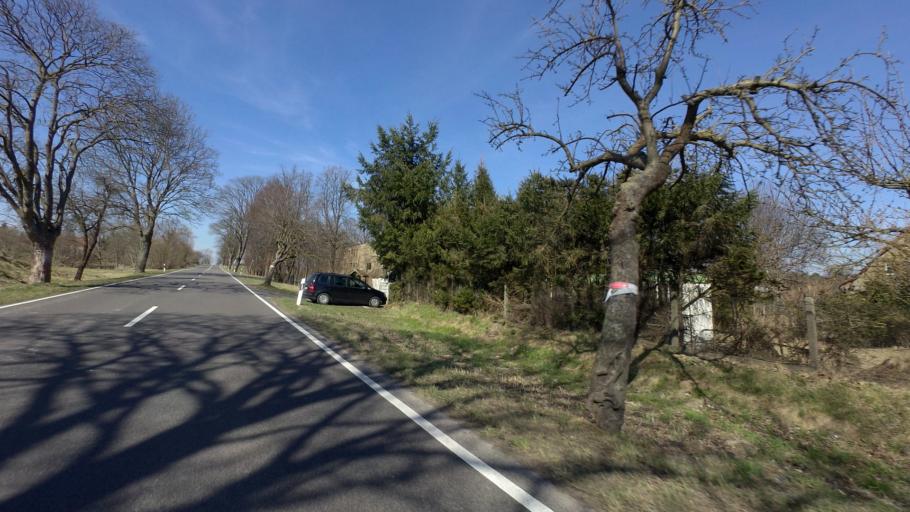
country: DE
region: Brandenburg
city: Protzel
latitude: 52.5957
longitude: 14.0261
